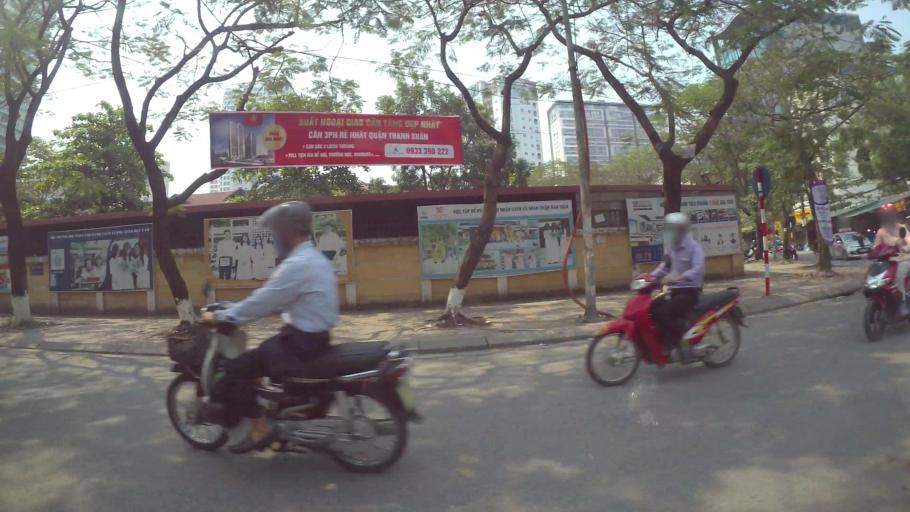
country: VN
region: Ha Noi
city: Thanh Xuan
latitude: 21.0037
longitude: 105.8070
